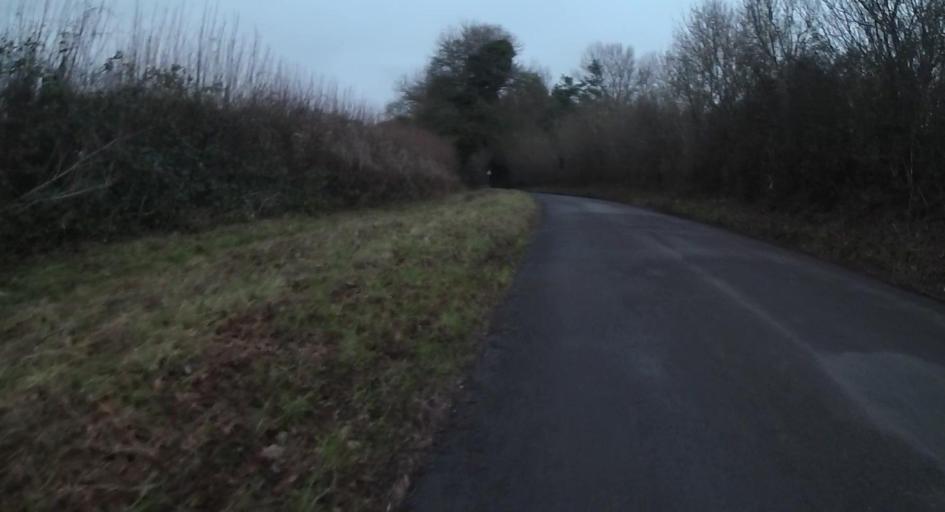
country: GB
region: England
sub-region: Hampshire
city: Four Marks
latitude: 51.0555
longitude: -1.0967
